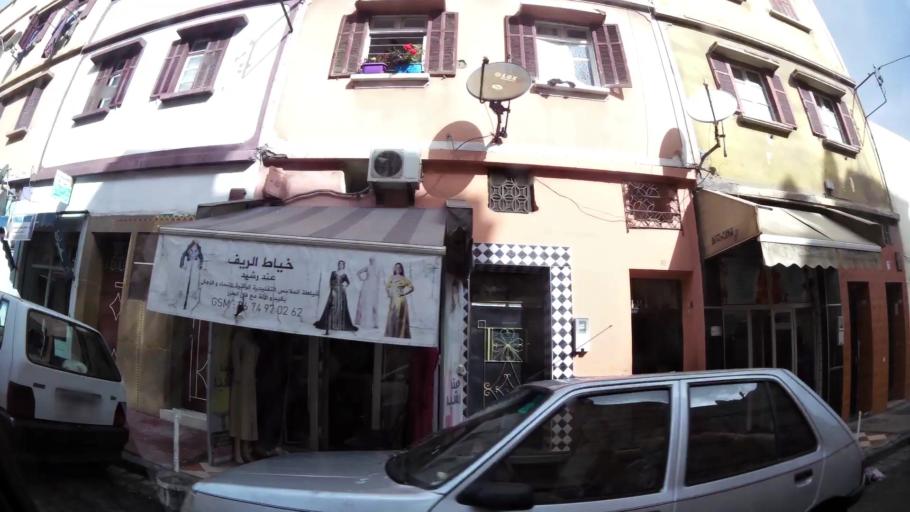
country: MA
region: Grand Casablanca
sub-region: Casablanca
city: Casablanca
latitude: 33.5671
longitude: -7.5889
